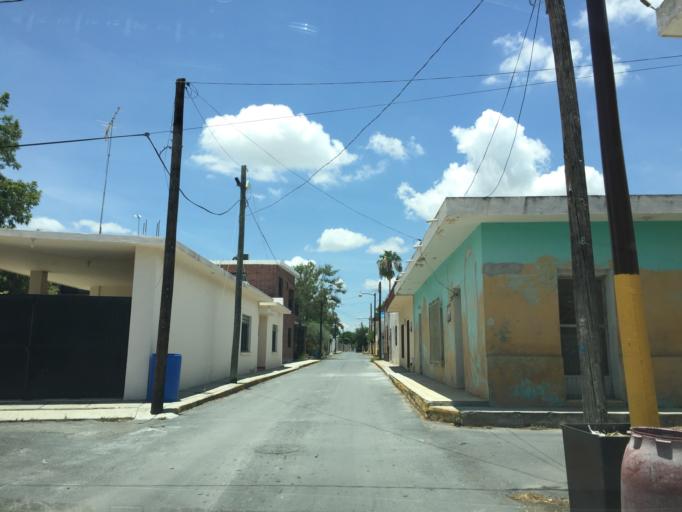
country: MX
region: Nuevo Leon
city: Marin
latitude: 25.8604
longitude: -99.9426
